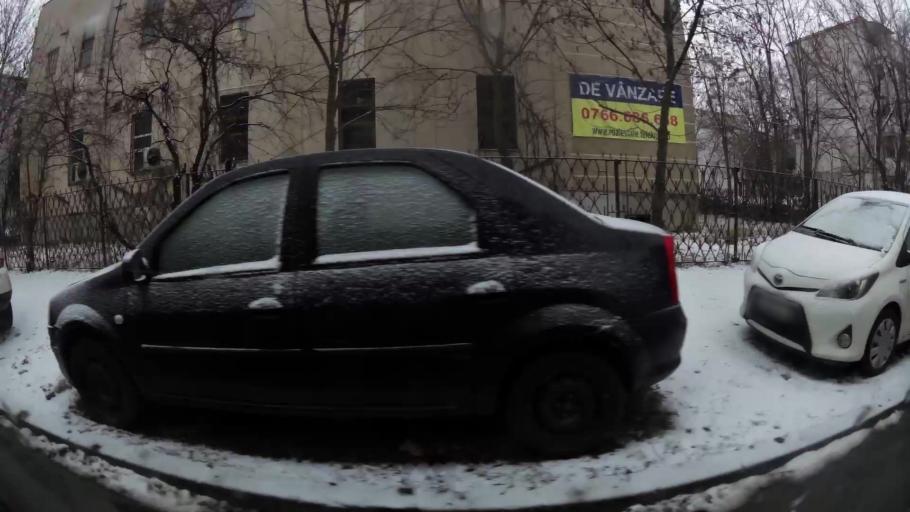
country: RO
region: Prahova
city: Ploiesti
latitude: 44.9344
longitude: 25.9924
